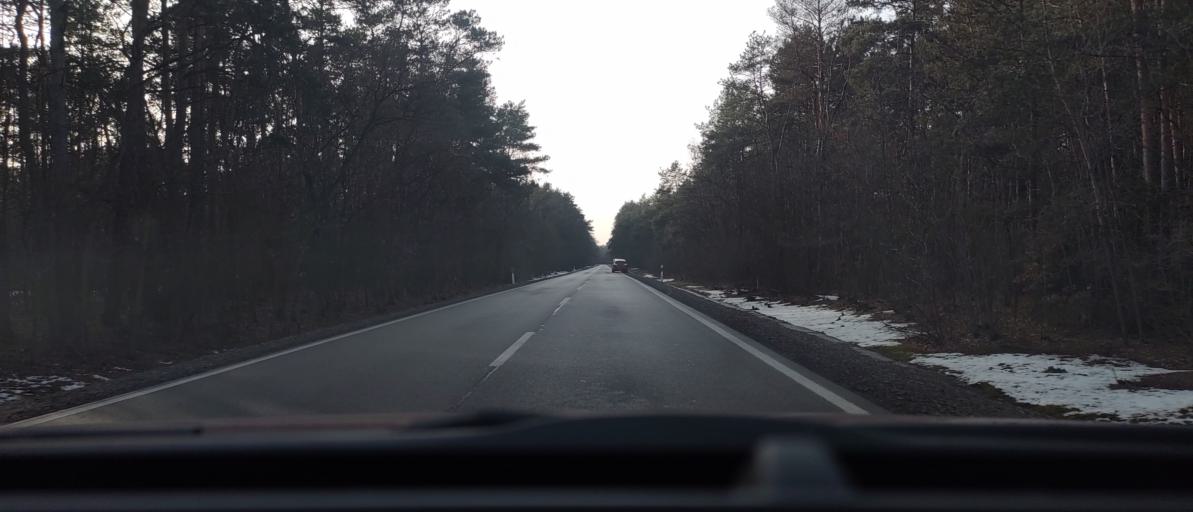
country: PL
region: Masovian Voivodeship
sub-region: Powiat bialobrzeski
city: Wysmierzyce
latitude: 51.6276
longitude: 20.8501
